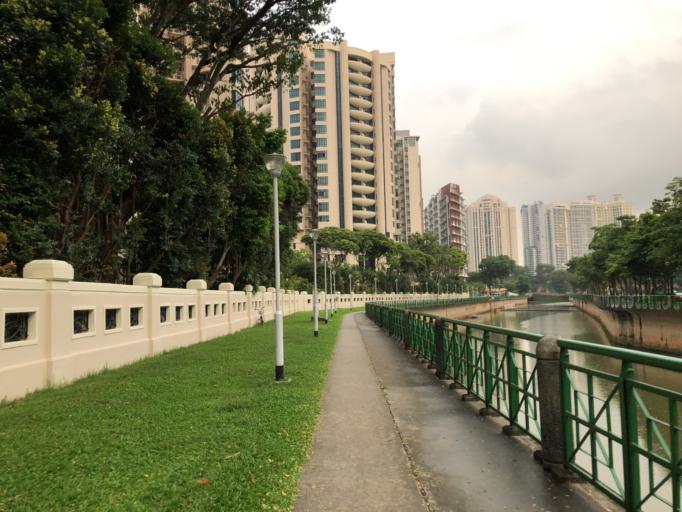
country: SG
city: Singapore
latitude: 1.2926
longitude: 103.8281
